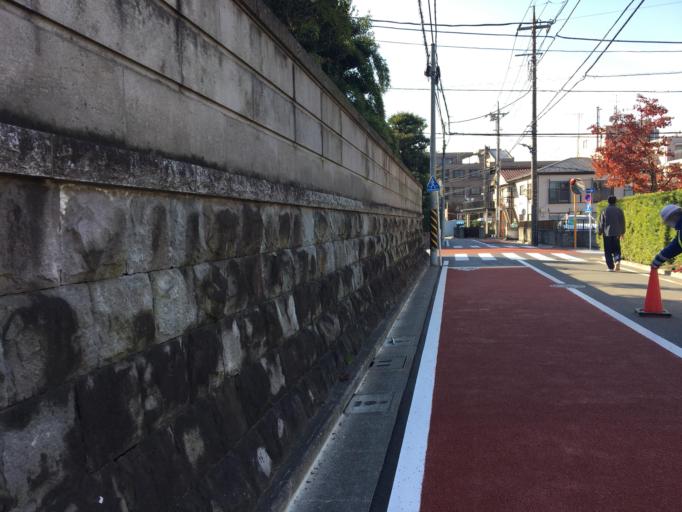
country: JP
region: Saitama
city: Wako
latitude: 35.7810
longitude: 139.6396
